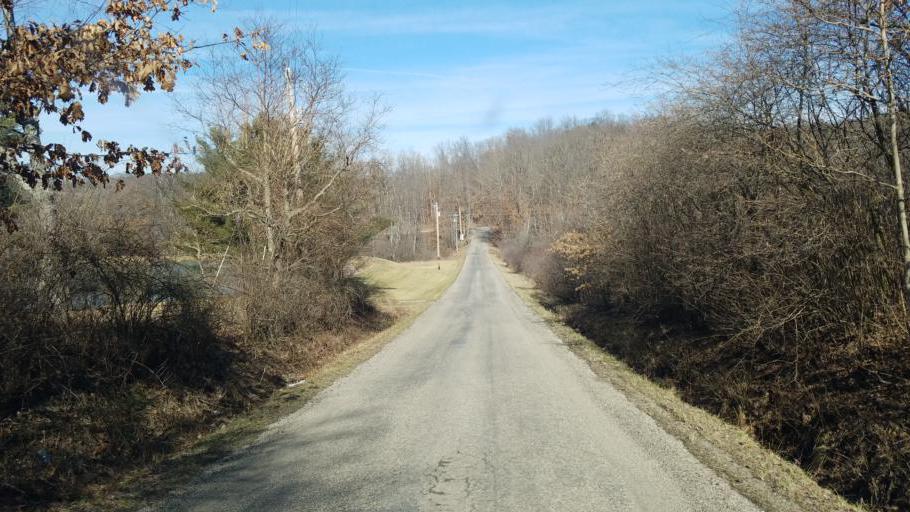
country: US
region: Ohio
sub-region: Ashland County
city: Loudonville
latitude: 40.5786
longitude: -82.3289
